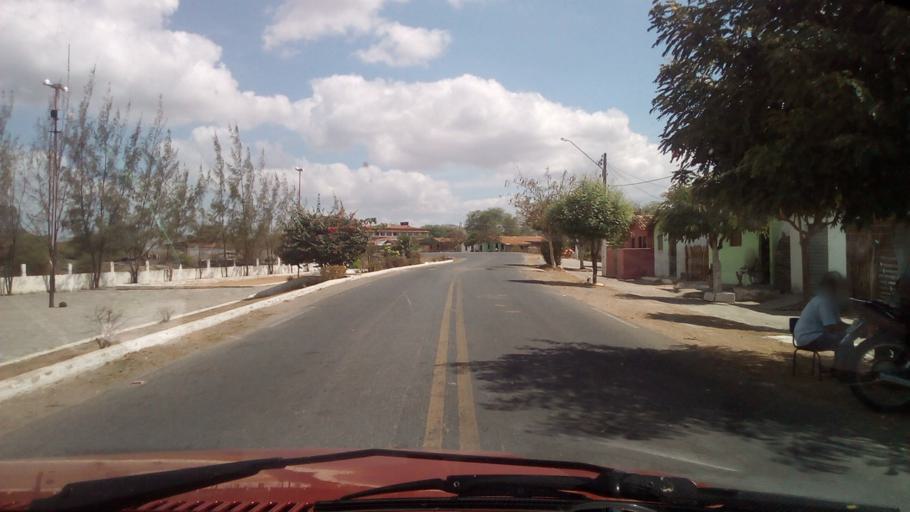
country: BR
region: Paraiba
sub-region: Dona Ines
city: Dona Ines
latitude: -6.5368
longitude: -35.6538
